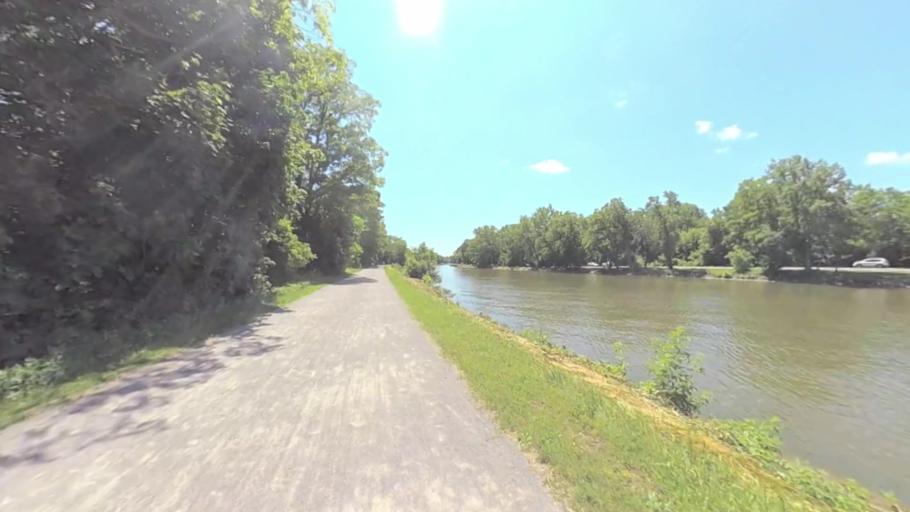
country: US
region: New York
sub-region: Monroe County
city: Pittsford
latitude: 43.0755
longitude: -77.4951
